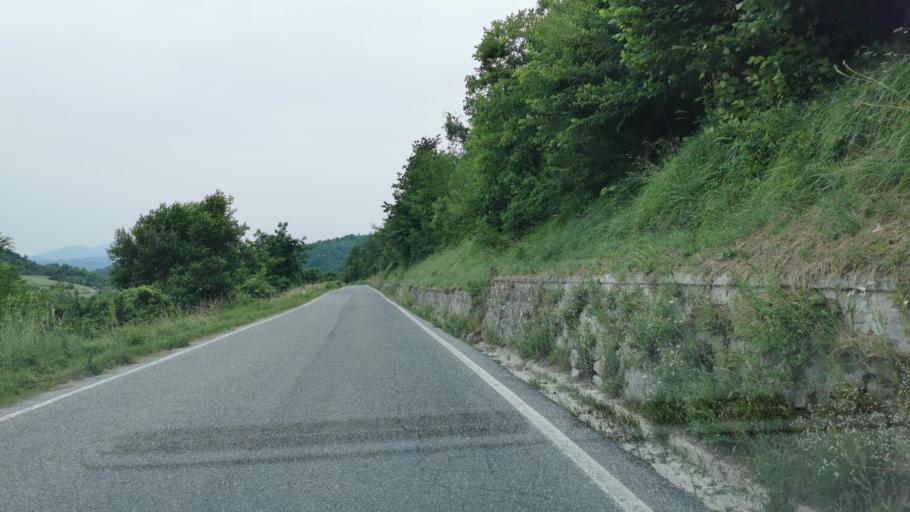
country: IT
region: Piedmont
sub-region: Provincia di Cuneo
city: Paroldo
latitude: 44.4251
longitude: 8.0564
